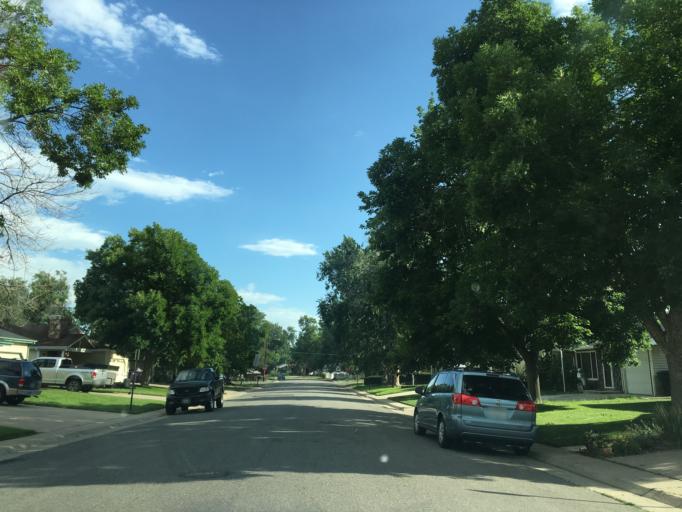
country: US
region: Colorado
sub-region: Jefferson County
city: Lakewood
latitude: 39.6903
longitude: -105.0410
